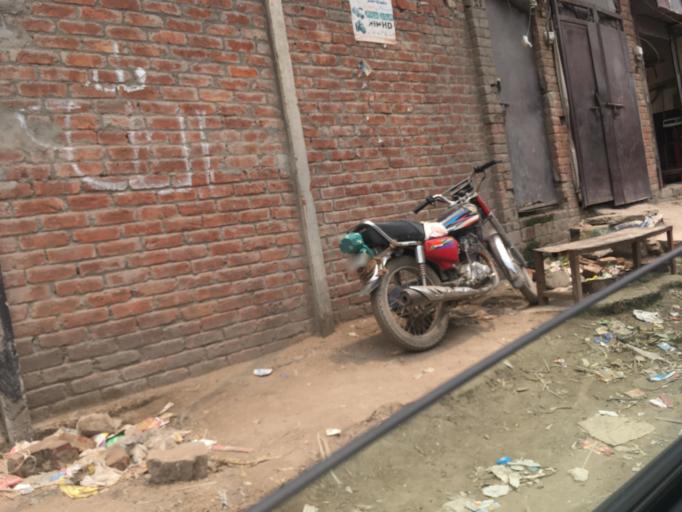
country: PK
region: Punjab
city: Lahore
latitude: 31.6139
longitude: 74.3509
